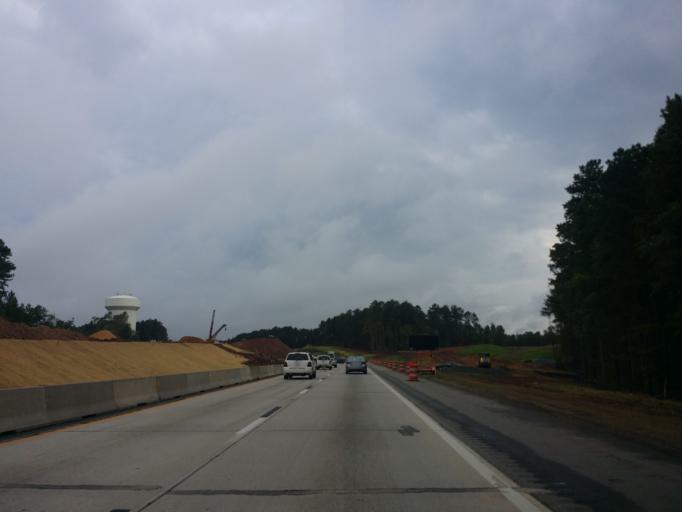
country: US
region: North Carolina
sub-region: Durham County
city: Durham
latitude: 35.9633
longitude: -78.8650
